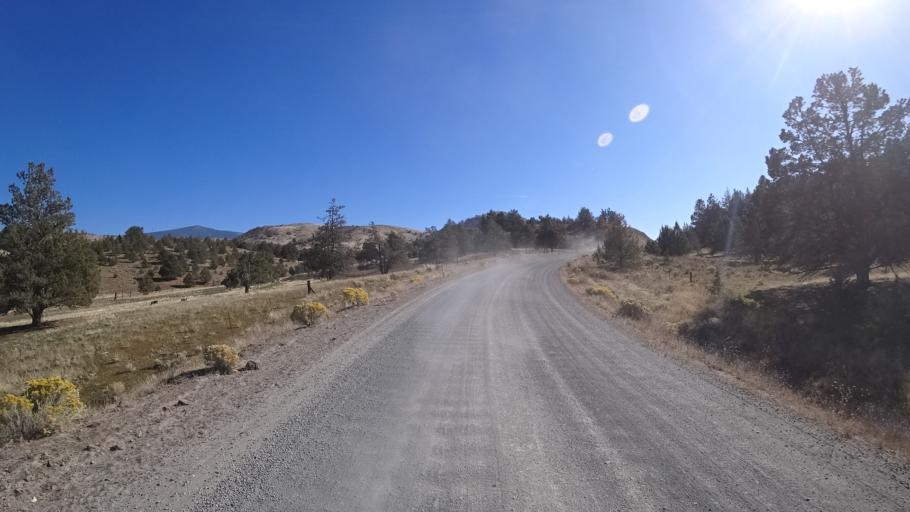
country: US
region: California
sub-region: Siskiyou County
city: Montague
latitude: 41.8078
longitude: -122.3724
